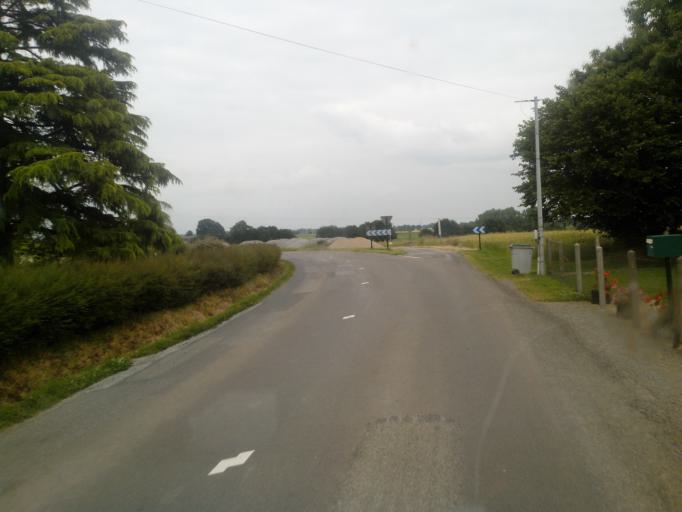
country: FR
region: Brittany
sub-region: Departement d'Ille-et-Vilaine
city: Noyal-sur-Vilaine
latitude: 48.1296
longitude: -1.5067
